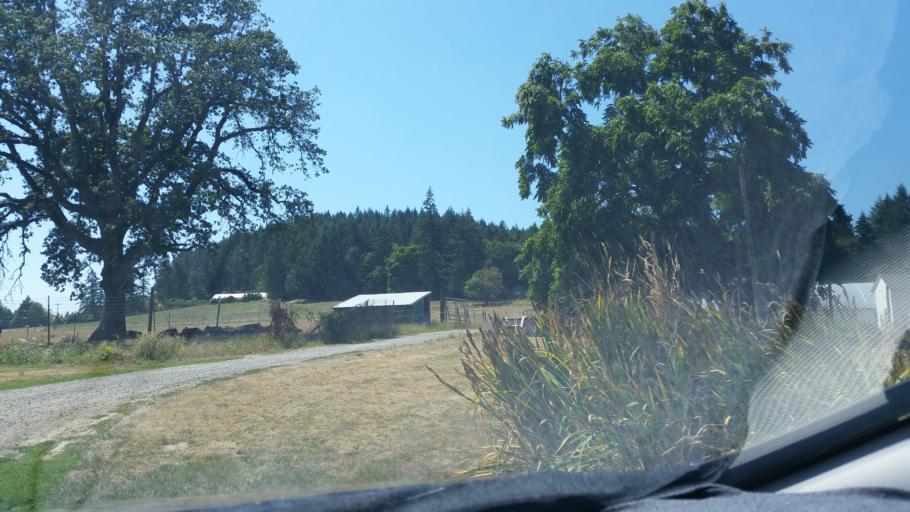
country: US
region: Oregon
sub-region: Clackamas County
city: Wilsonville
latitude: 45.2571
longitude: -122.8426
